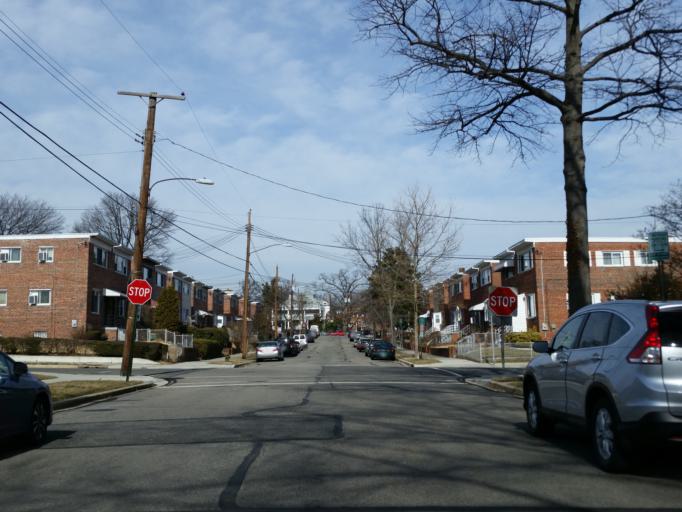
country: US
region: Maryland
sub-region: Montgomery County
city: Silver Spring
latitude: 38.9812
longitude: -77.0244
